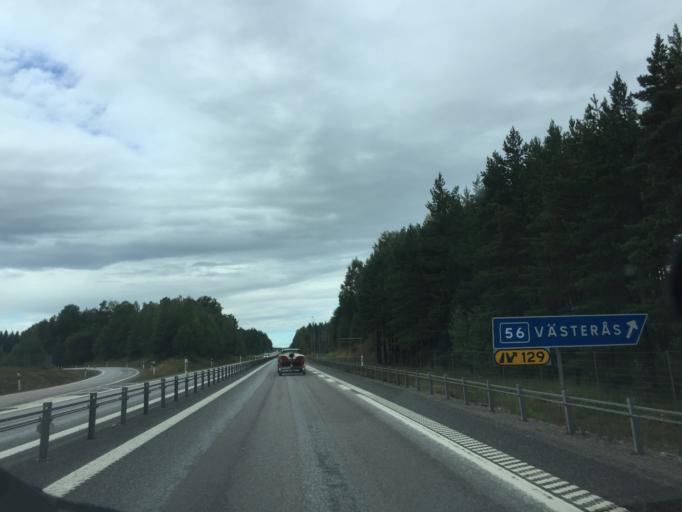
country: SE
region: Soedermanland
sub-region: Eskilstuna Kommun
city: Hallbybrunn
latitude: 59.4067
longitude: 16.3830
